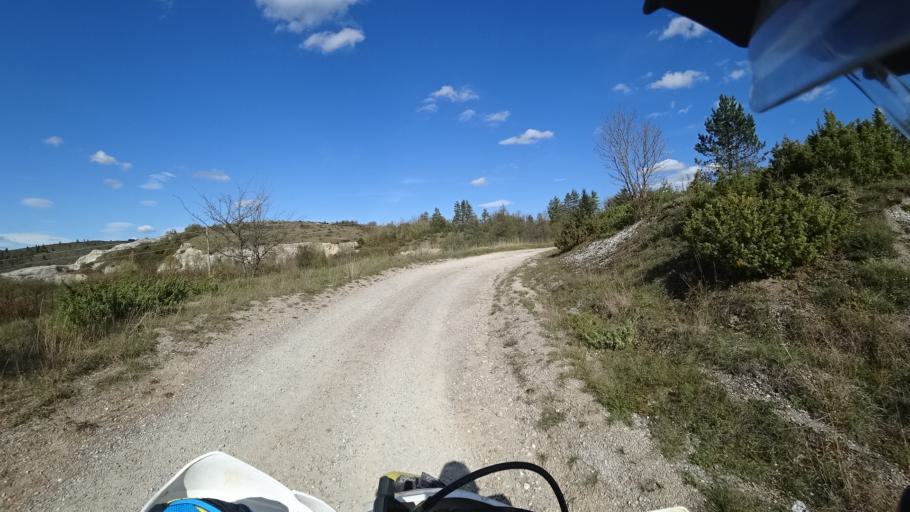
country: HR
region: Karlovacka
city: Plaski
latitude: 45.0747
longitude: 15.3524
